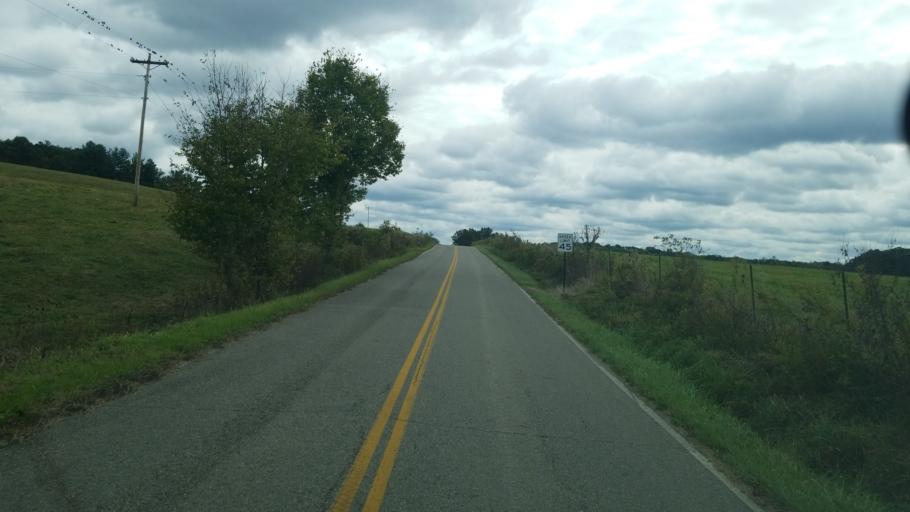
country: US
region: Ohio
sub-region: Jackson County
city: Jackson
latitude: 39.1377
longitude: -82.6497
